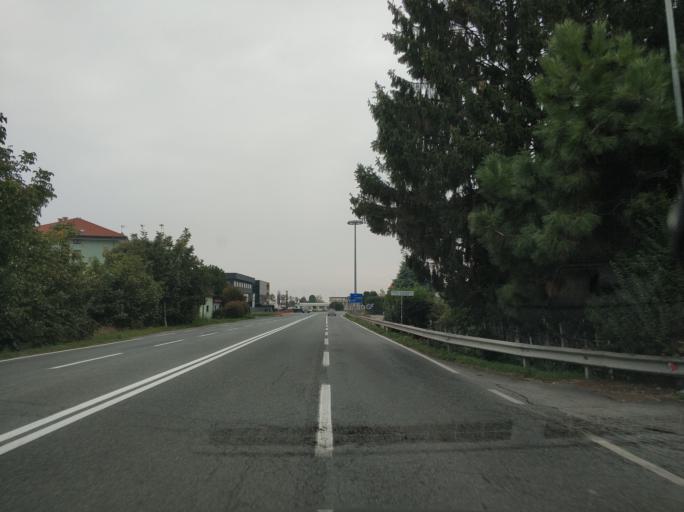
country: IT
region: Piedmont
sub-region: Provincia di Torino
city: Cirie
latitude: 45.2231
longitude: 7.6053
